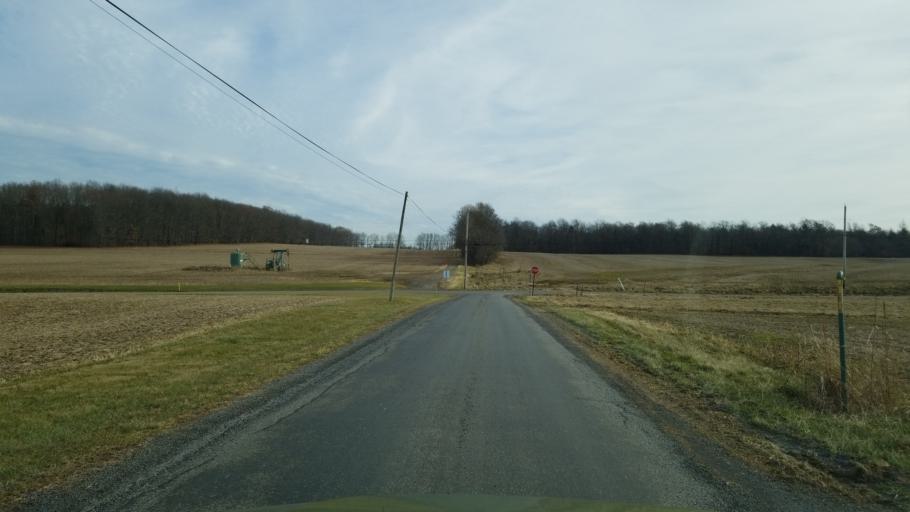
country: US
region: Pennsylvania
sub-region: Indiana County
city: Johnsonburg
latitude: 40.9394
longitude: -78.8714
